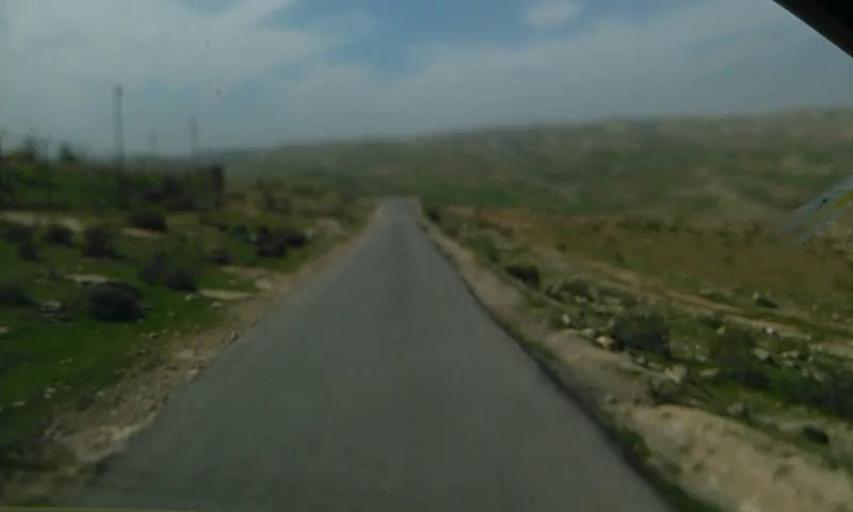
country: PS
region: West Bank
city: Khallat al Mayyah
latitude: 31.4344
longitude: 35.1841
